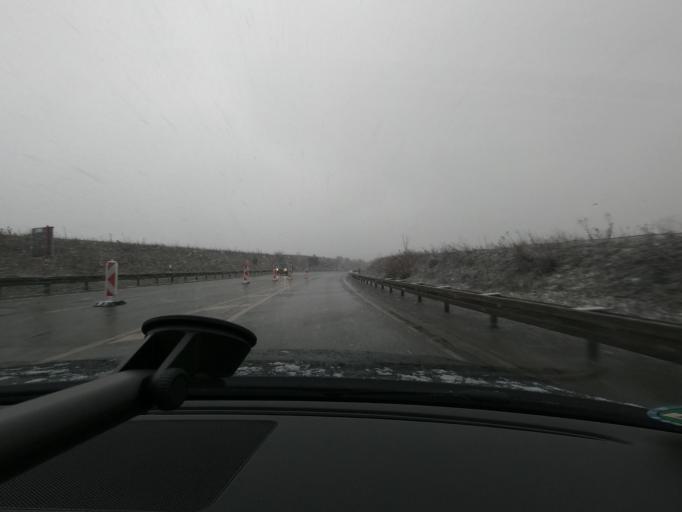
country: DE
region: Thuringia
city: Dingelstadt
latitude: 51.3282
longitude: 10.3269
